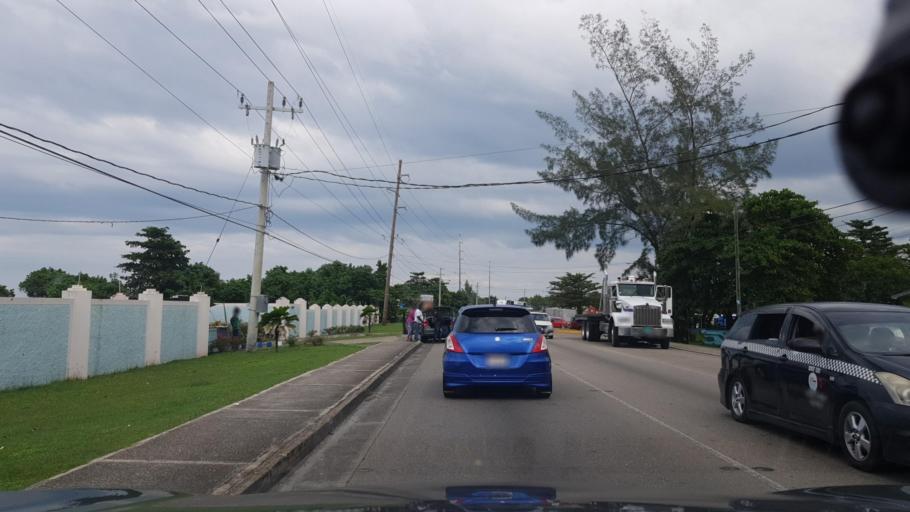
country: JM
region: Saint Ann
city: Runaway Bay
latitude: 18.4681
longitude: -77.3007
